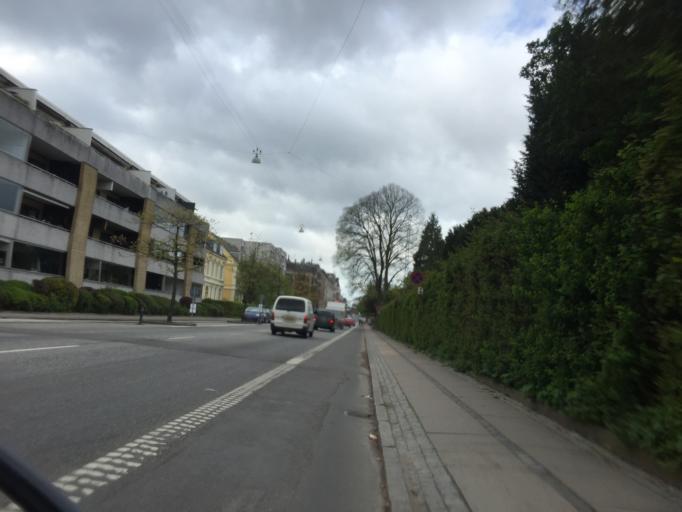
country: DK
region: Capital Region
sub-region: Frederiksberg Kommune
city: Frederiksberg
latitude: 55.6738
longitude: 12.5319
